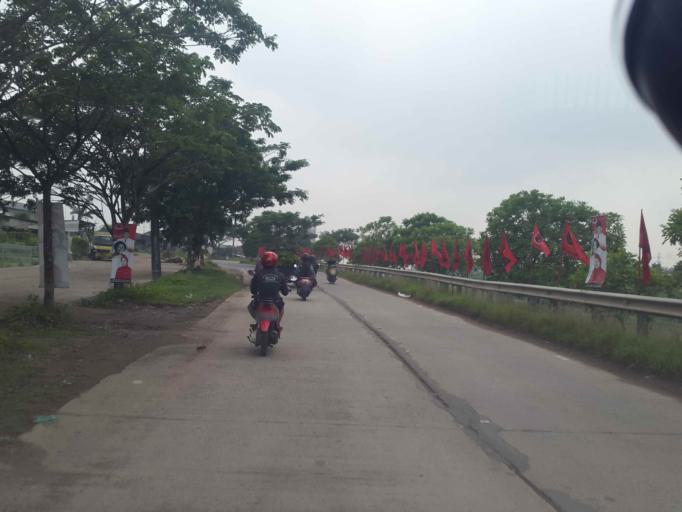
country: ID
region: West Java
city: Cikarang
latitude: -6.3302
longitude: 107.1738
